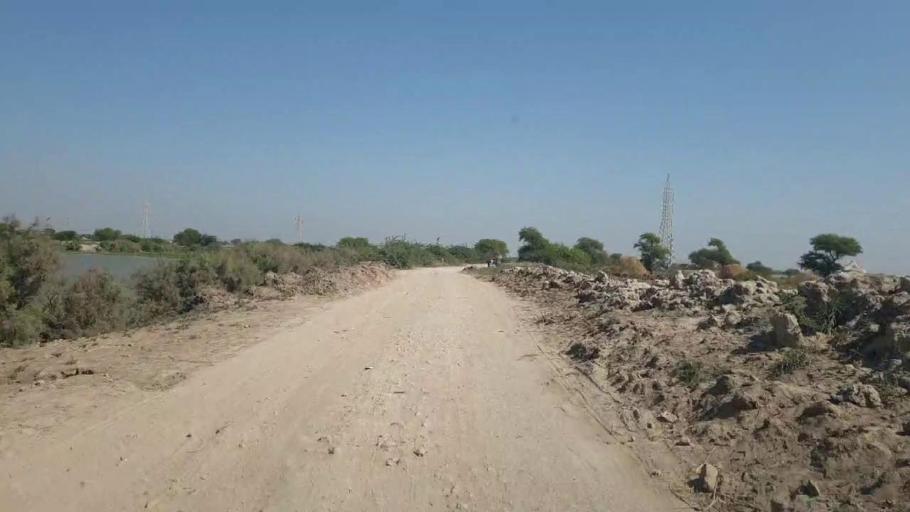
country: PK
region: Sindh
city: Talhar
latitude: 24.7969
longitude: 68.8117
